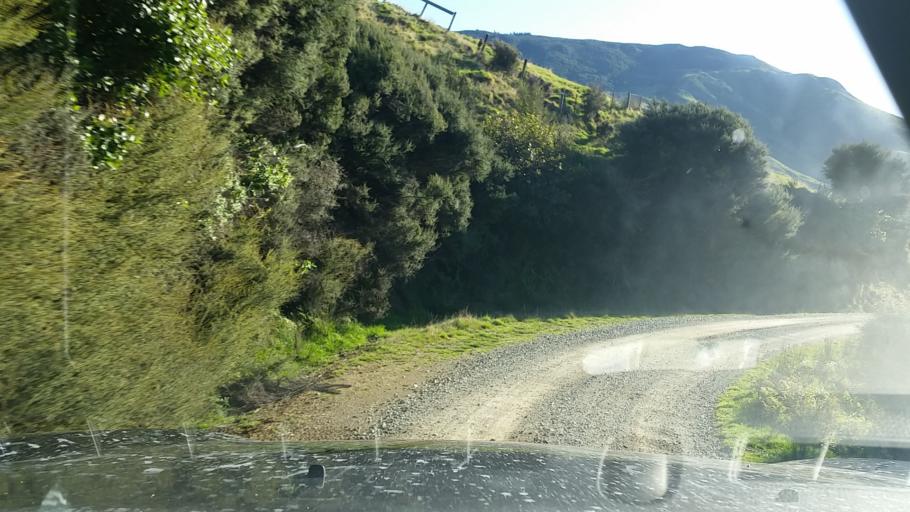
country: NZ
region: Marlborough
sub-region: Marlborough District
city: Picton
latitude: -41.0218
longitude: 174.1413
